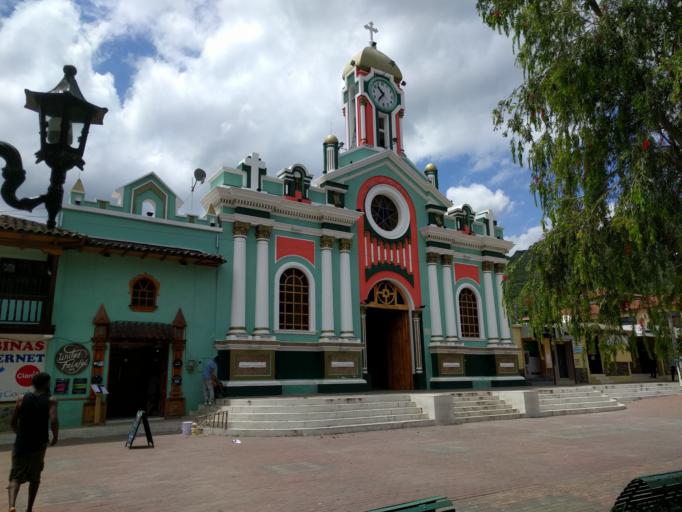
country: EC
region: Loja
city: Loja
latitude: -4.2609
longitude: -79.2225
